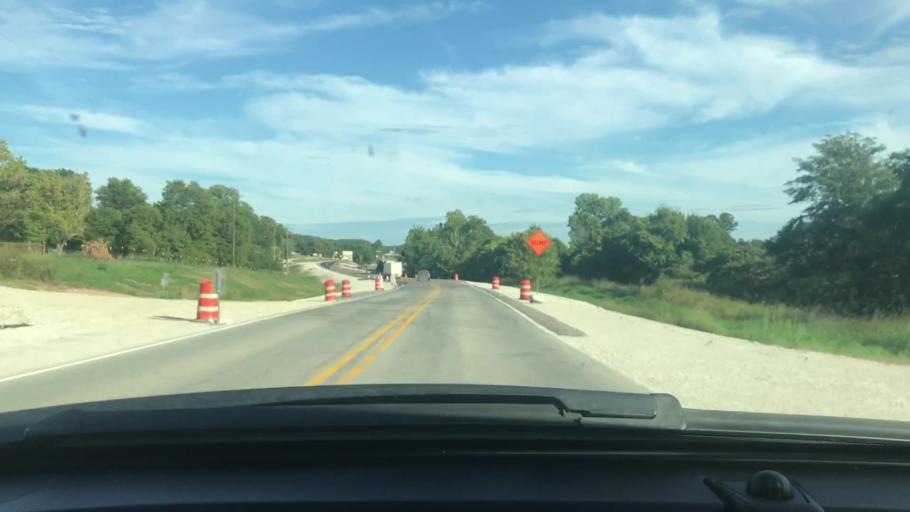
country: US
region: Arkansas
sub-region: Sharp County
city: Cherokee Village
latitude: 36.3049
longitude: -91.4507
